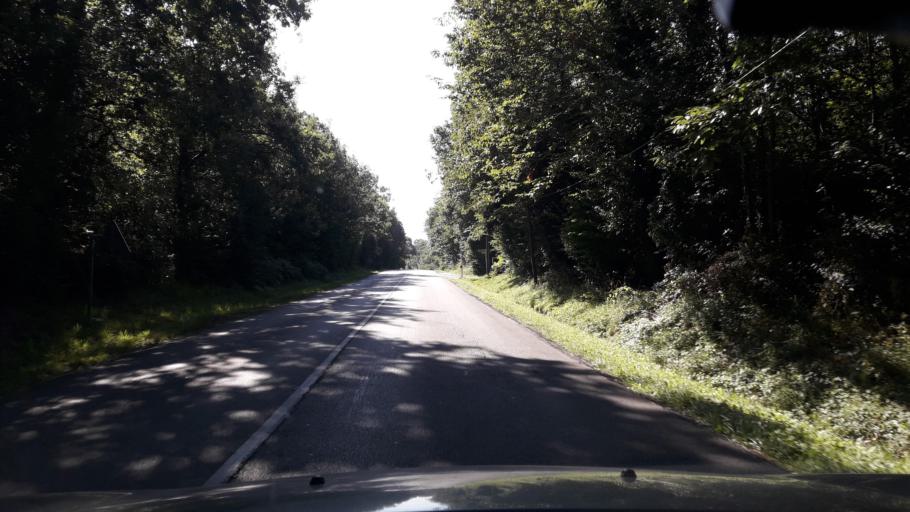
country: FR
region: Poitou-Charentes
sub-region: Departement de la Charente-Maritime
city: Etaules
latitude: 45.7245
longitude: -1.0891
